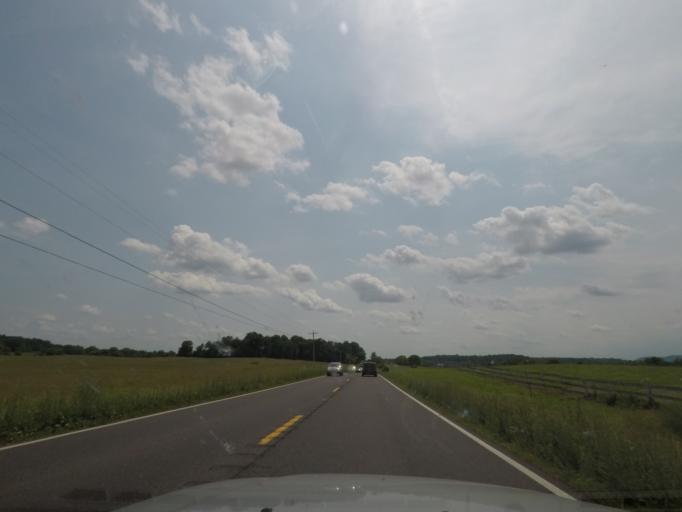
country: US
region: Virginia
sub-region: Culpeper County
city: Merrimac
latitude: 38.4207
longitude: -78.0444
